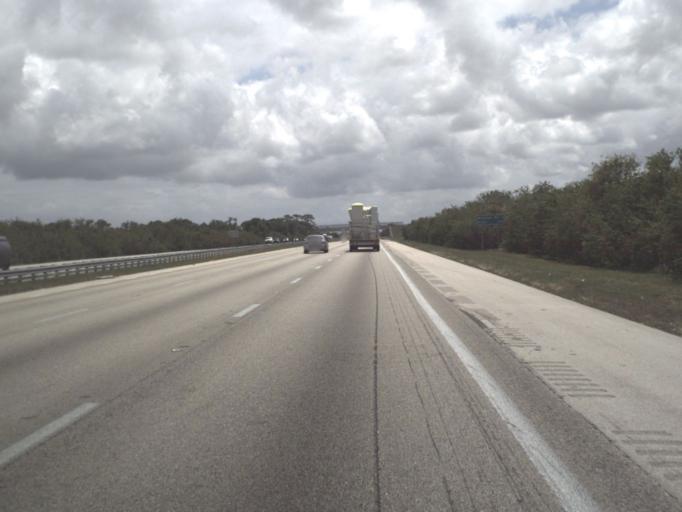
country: US
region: Florida
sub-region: Brevard County
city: Rockledge
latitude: 28.2730
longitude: -80.7311
